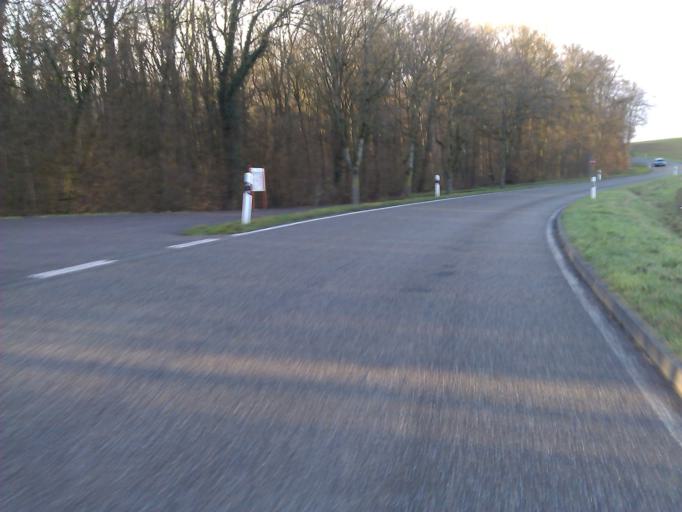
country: DE
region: Baden-Wuerttemberg
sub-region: Regierungsbezirk Stuttgart
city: Oedheim
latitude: 49.2462
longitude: 9.2426
